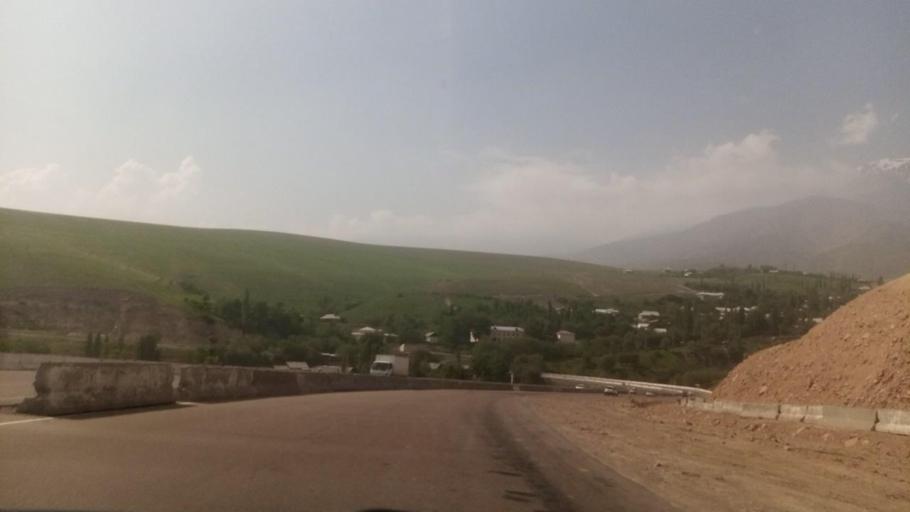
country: UZ
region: Toshkent
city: Angren
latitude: 41.0702
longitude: 70.2368
